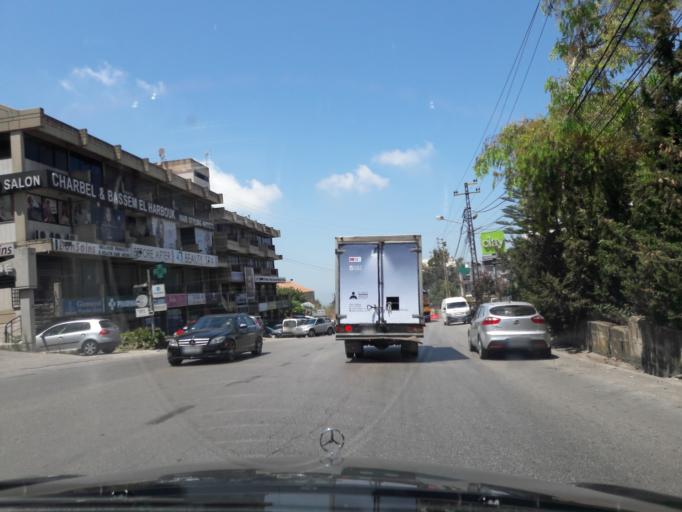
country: LB
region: Mont-Liban
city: Djounie
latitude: 33.9211
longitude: 35.6336
